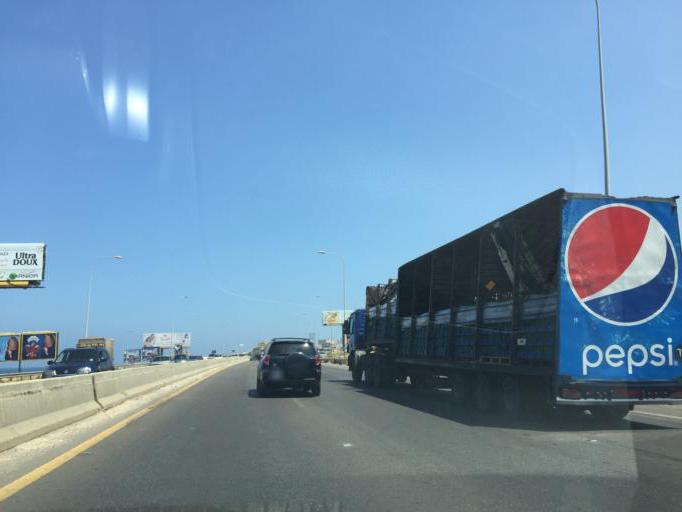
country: LB
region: Liban-Sud
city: Sidon
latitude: 33.6229
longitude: 35.4023
